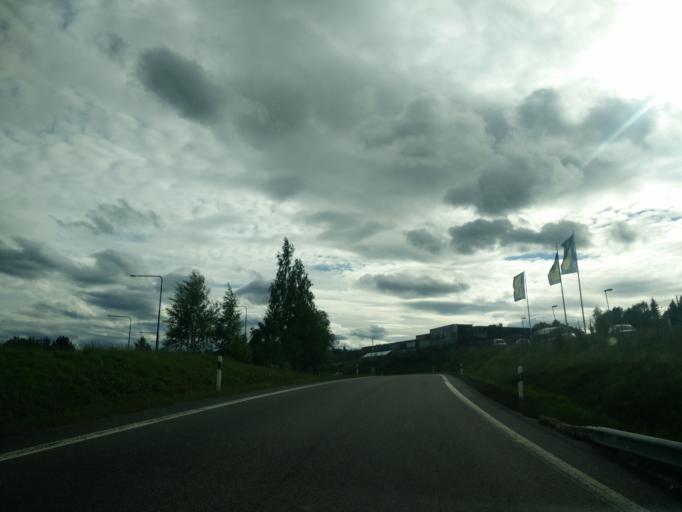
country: SE
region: Vaesternorrland
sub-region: Sundsvalls Kommun
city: Johannedal
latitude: 62.4130
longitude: 17.3396
